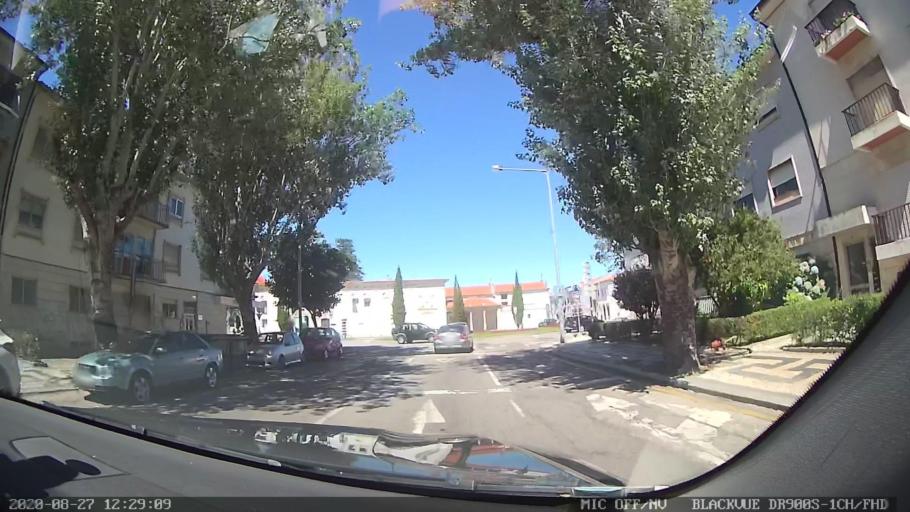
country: PT
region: Aveiro
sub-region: Aveiro
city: Aveiro
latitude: 40.6386
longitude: -8.6500
